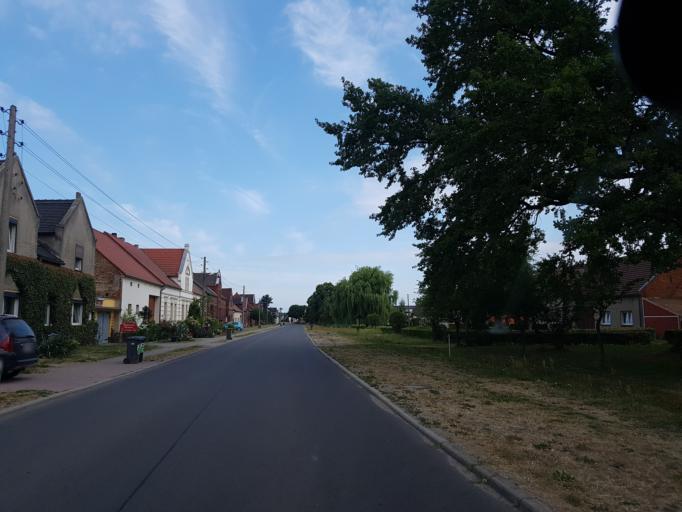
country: DE
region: Brandenburg
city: Luckau
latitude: 51.8375
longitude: 13.6401
